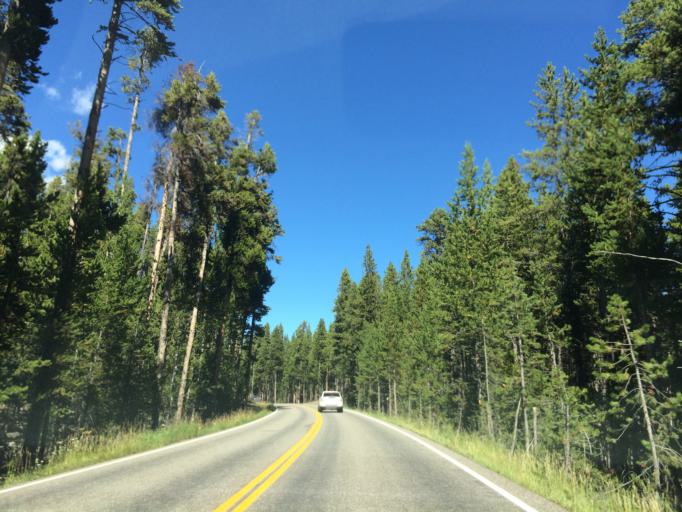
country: US
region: Montana
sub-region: Gallatin County
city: West Yellowstone
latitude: 44.5767
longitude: -110.3801
